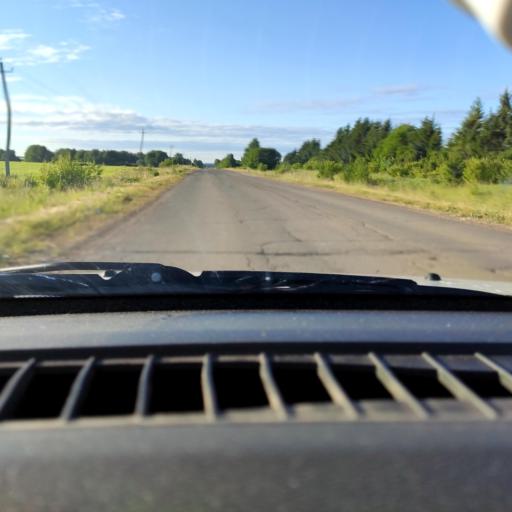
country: RU
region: Perm
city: Uinskoye
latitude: 57.1012
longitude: 56.5406
